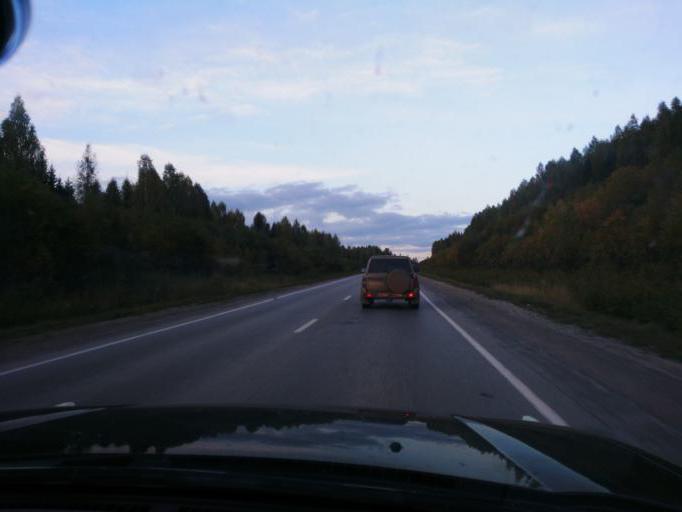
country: RU
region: Perm
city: Polazna
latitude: 58.2987
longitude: 56.5314
